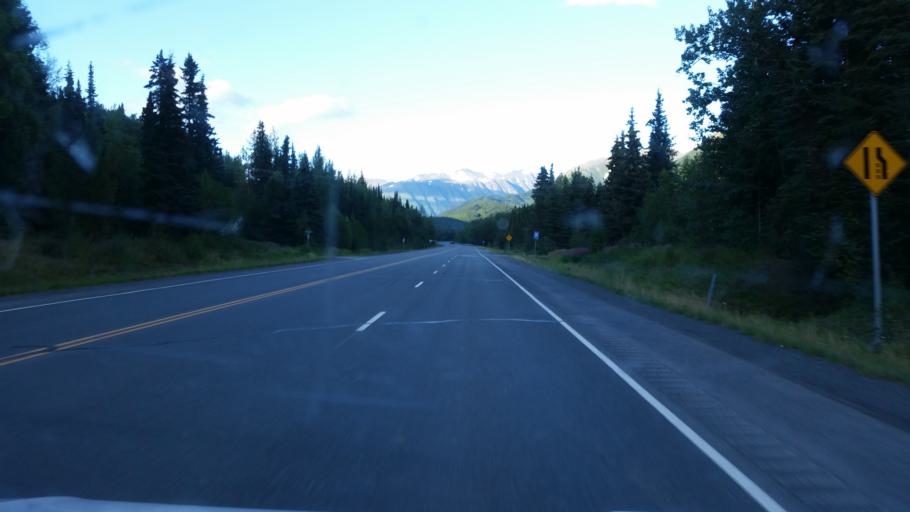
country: US
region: Alaska
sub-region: Kenai Peninsula Borough
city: Bear Creek
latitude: 60.4894
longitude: -149.7169
